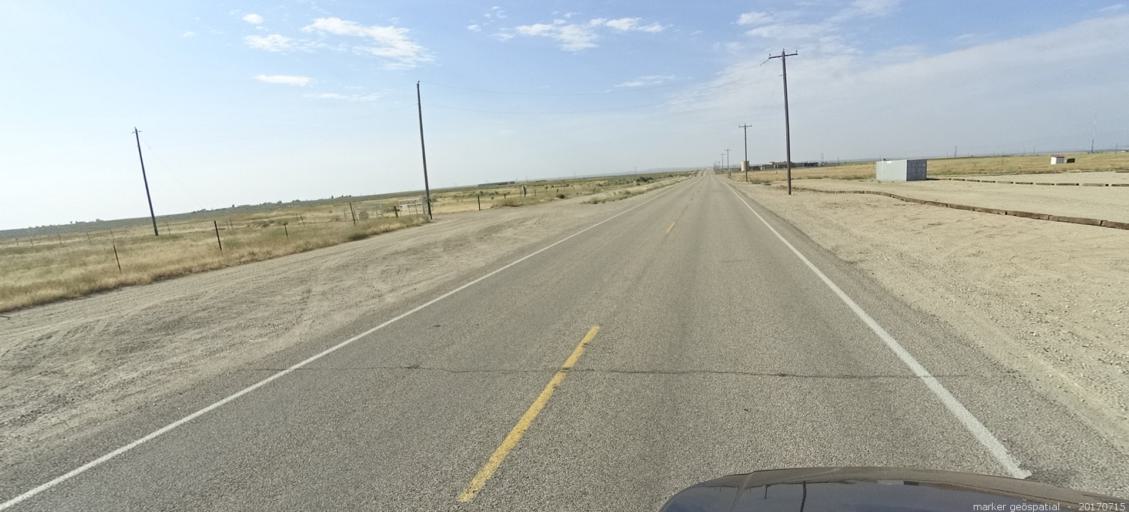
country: US
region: Idaho
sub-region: Ada County
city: Boise
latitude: 43.4693
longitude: -116.2343
